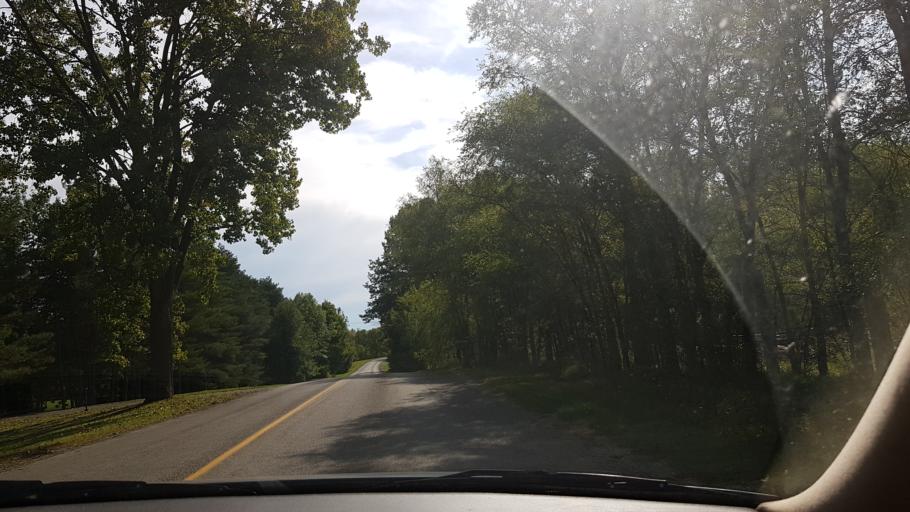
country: CA
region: Ontario
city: Delaware
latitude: 42.9135
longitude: -81.4698
